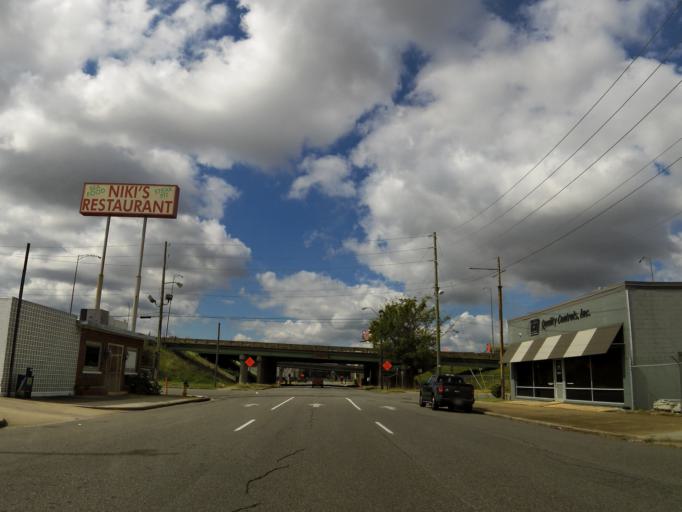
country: US
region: Alabama
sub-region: Jefferson County
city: Birmingham
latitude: 33.5097
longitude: -86.8183
